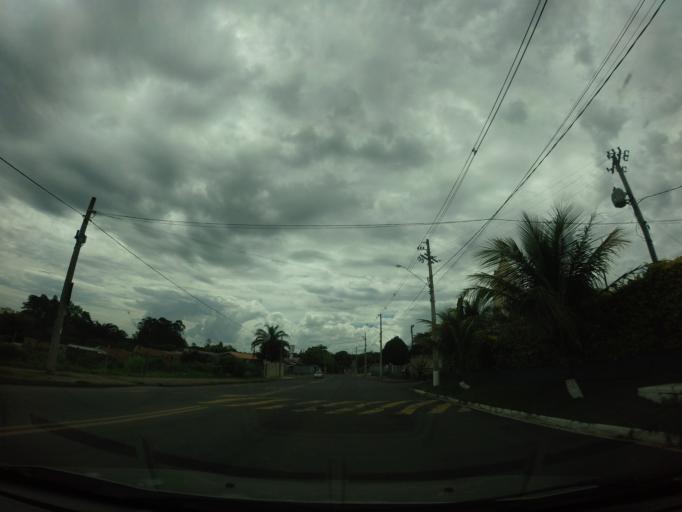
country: BR
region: Sao Paulo
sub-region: Piracicaba
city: Piracicaba
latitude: -22.7523
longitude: -47.6129
